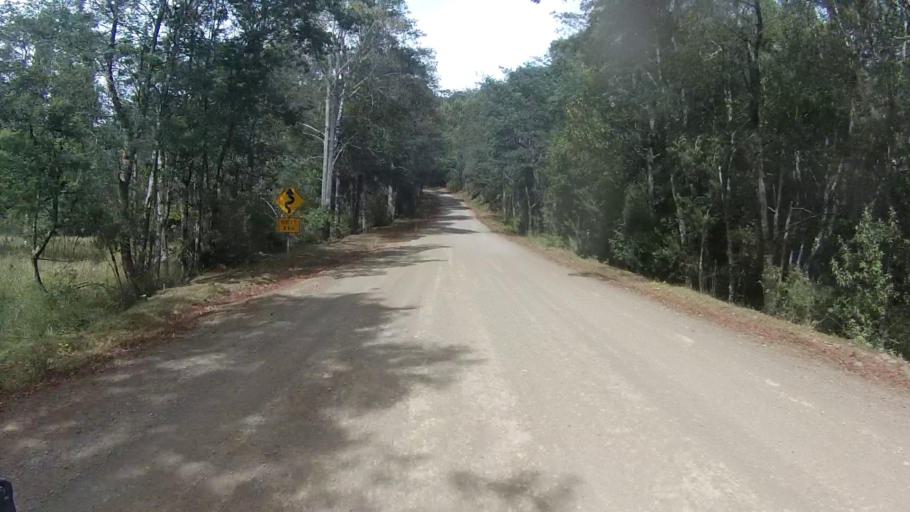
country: AU
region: Tasmania
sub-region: Sorell
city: Sorell
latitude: -42.6929
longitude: 147.8620
